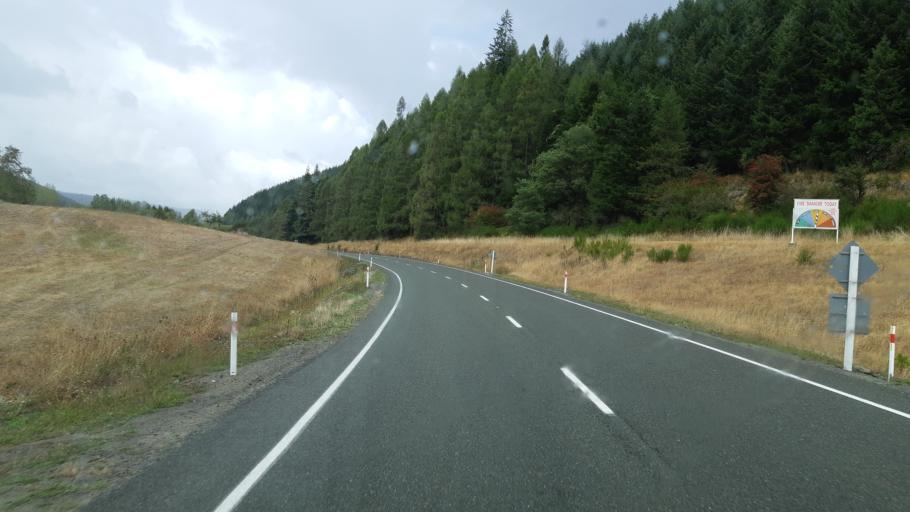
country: NZ
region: Tasman
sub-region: Tasman District
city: Wakefield
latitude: -41.4739
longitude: 172.8457
